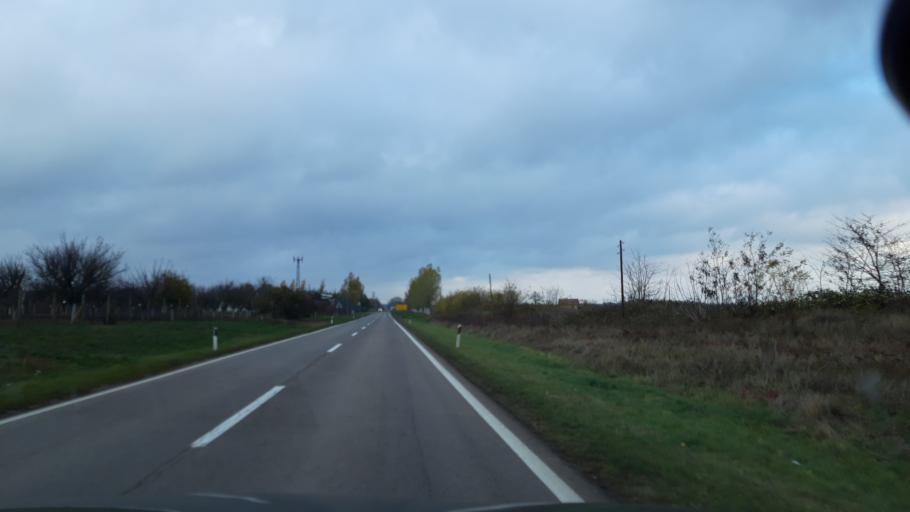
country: RS
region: Autonomna Pokrajina Vojvodina
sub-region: Severnobanatski Okrug
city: Novi Knezevac
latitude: 46.0203
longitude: 20.0958
